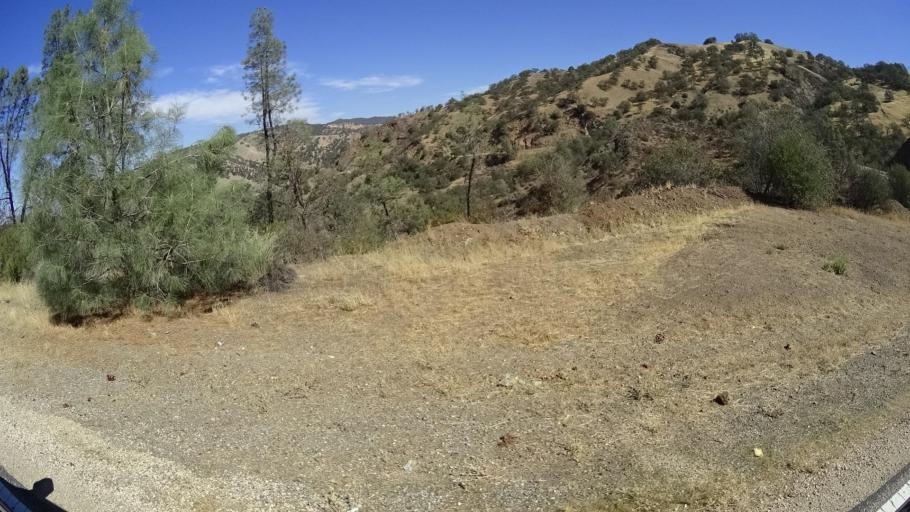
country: US
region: California
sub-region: Monterey County
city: King City
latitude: 36.1878
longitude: -120.7502
